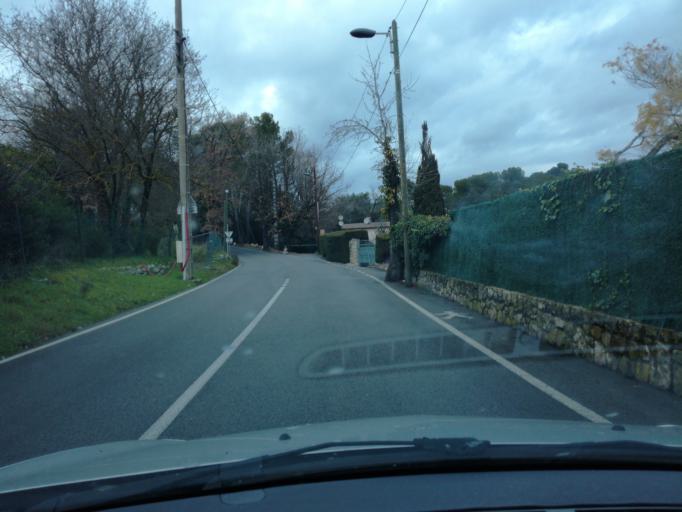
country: FR
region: Provence-Alpes-Cote d'Azur
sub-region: Departement des Alpes-Maritimes
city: Mougins
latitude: 43.6047
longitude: 6.9860
